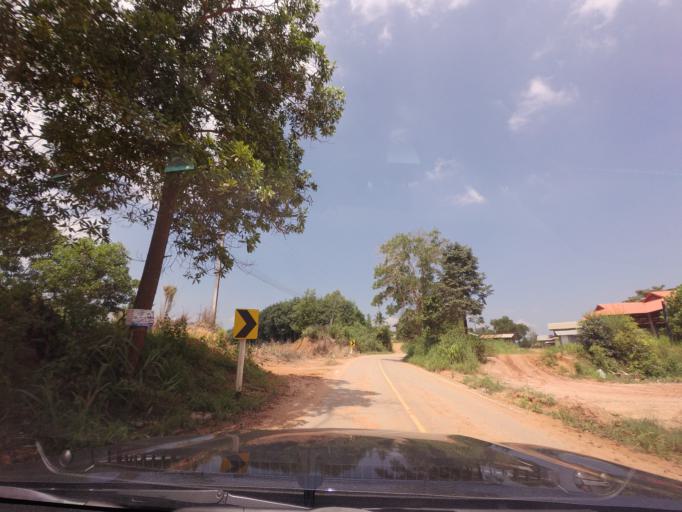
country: TH
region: Loei
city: Na Haeo
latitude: 17.5232
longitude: 100.8778
